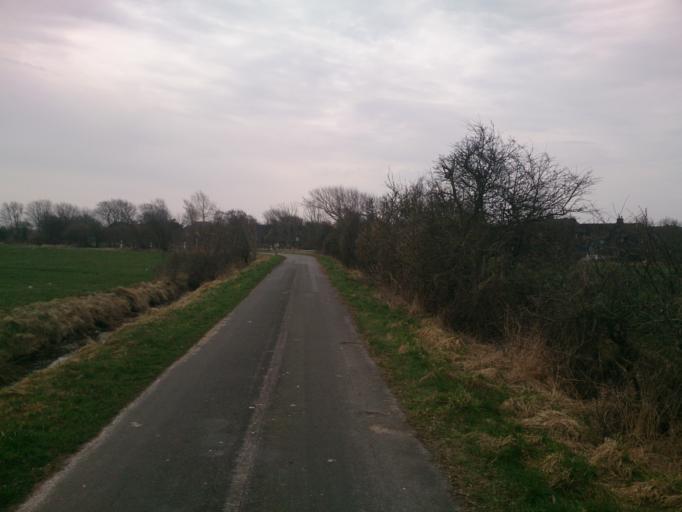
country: DE
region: Schleswig-Holstein
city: Utersum
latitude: 54.7173
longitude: 8.4077
